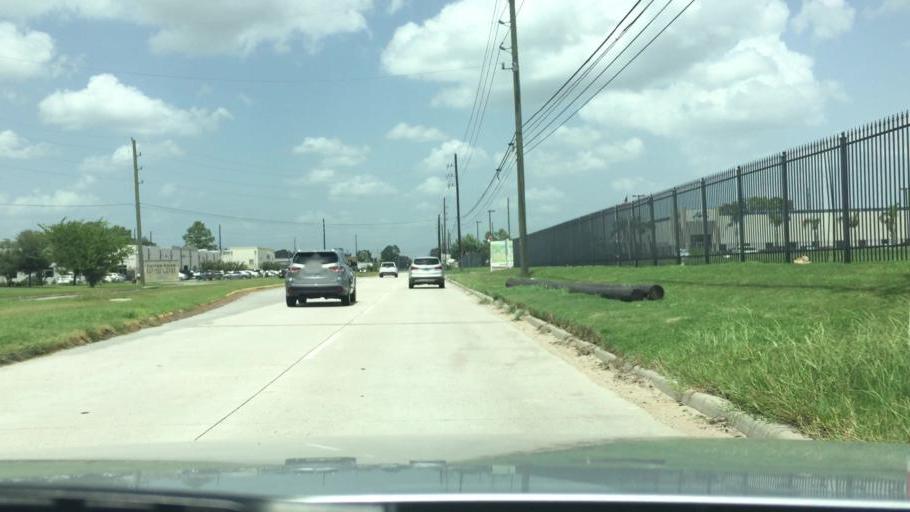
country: US
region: Texas
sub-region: Harris County
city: Hudson
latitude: 29.9576
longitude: -95.5257
